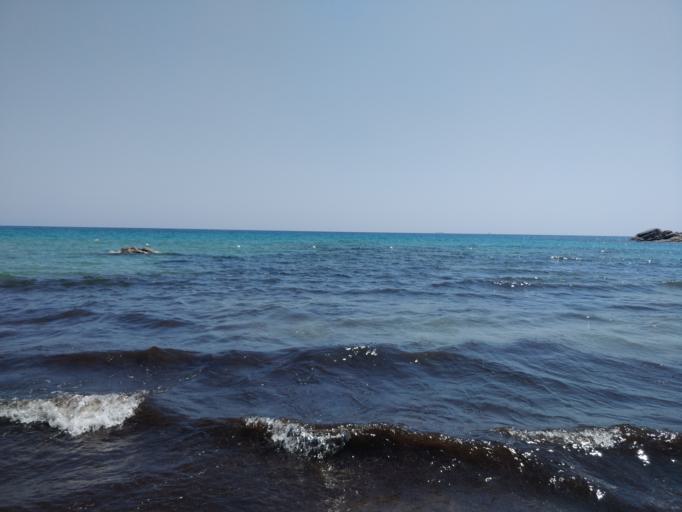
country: IT
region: Sardinia
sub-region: Provincia di Ogliastra
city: Tortoli
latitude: 39.8818
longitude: 9.6811
